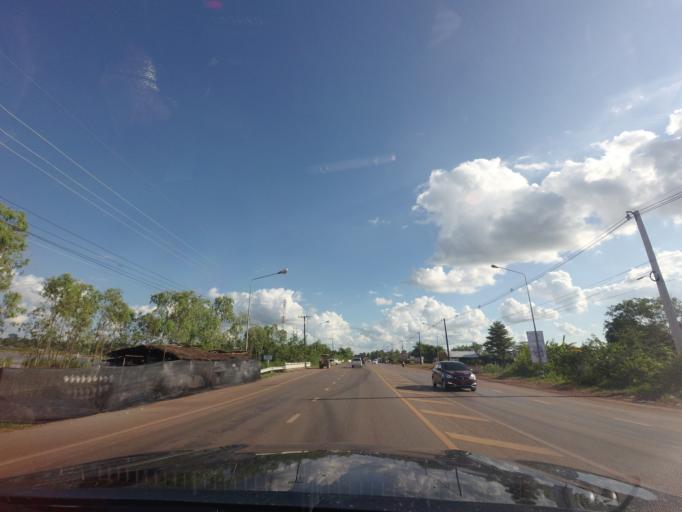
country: TH
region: Changwat Udon Thani
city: Ban Dung
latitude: 17.7137
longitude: 103.2502
